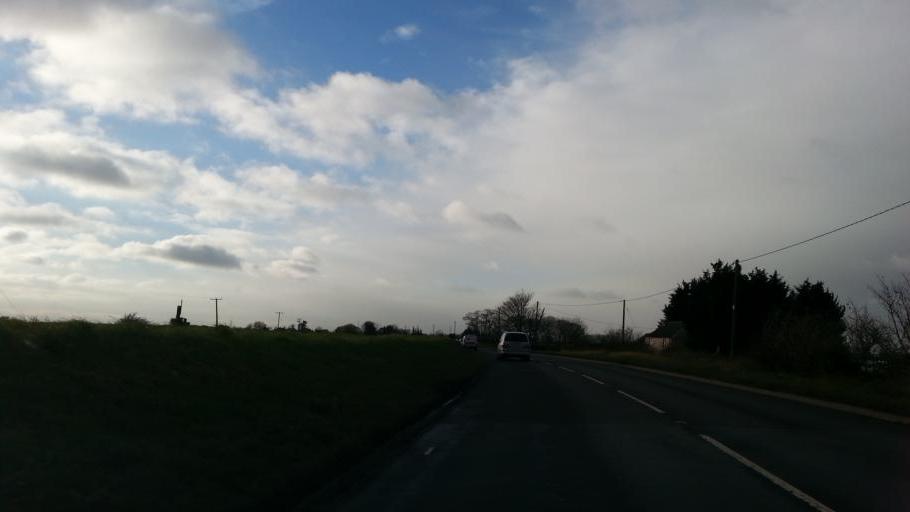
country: GB
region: England
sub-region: Norfolk
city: Downham Market
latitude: 52.5865
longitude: 0.3213
